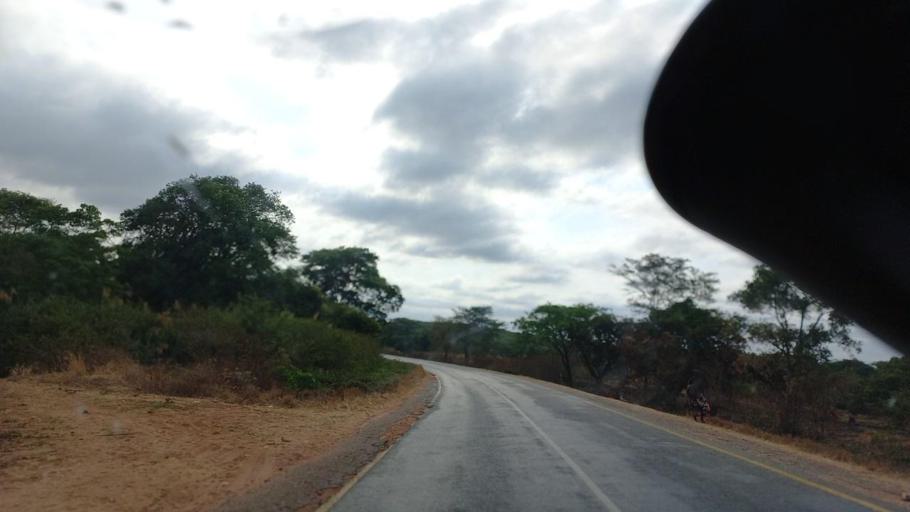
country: ZM
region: Lusaka
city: Chongwe
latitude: -15.2717
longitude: 28.9043
